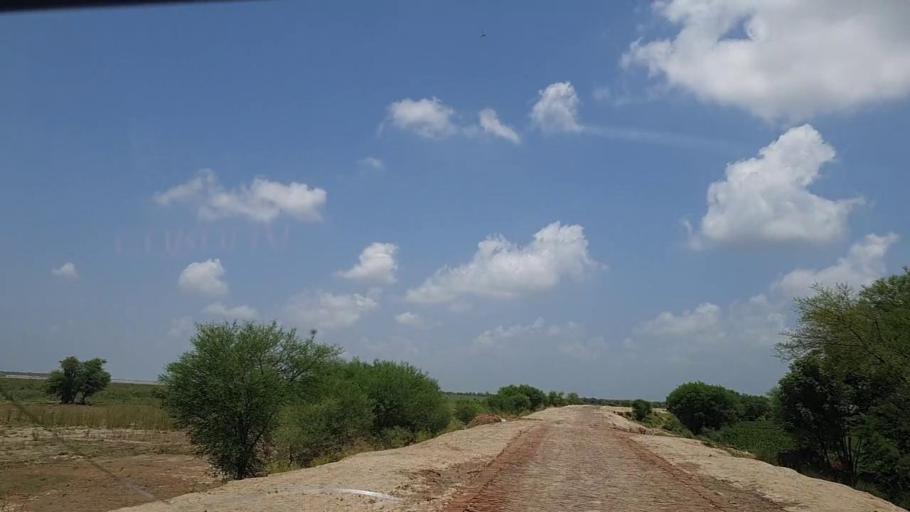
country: PK
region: Sindh
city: Tharu Shah
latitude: 26.9352
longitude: 67.9970
